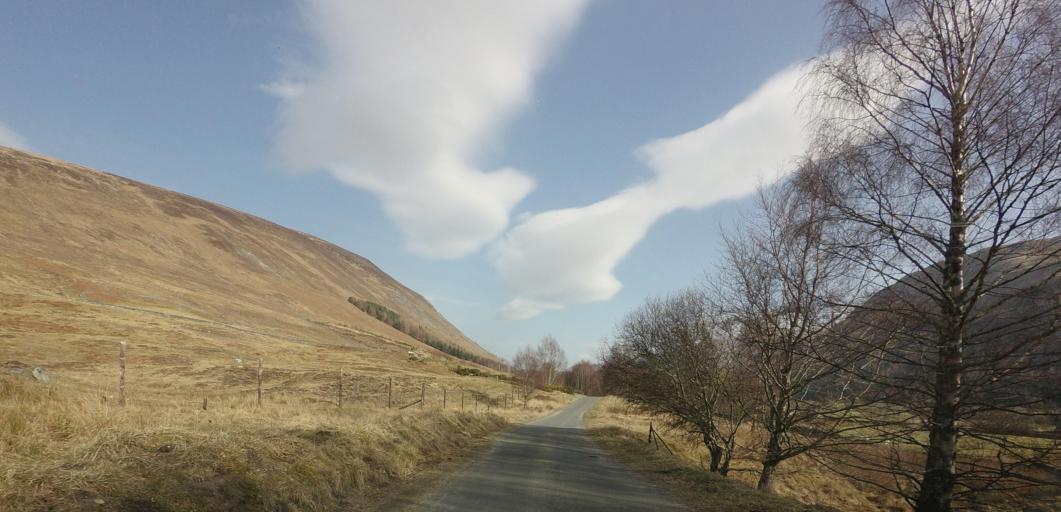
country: GB
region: Scotland
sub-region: Stirling
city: Callander
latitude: 56.5988
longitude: -4.3012
